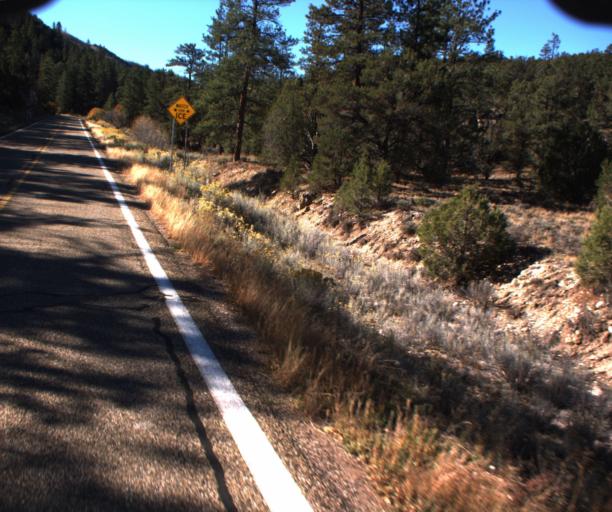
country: US
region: Arizona
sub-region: Coconino County
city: Fredonia
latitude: 36.7411
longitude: -112.1247
